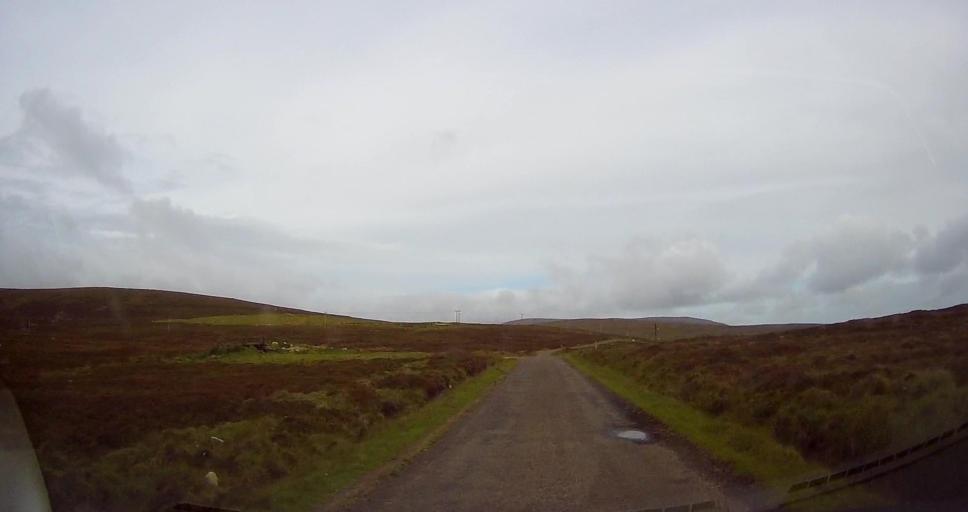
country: GB
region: Scotland
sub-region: Orkney Islands
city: Stromness
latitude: 58.8538
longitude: -3.2079
